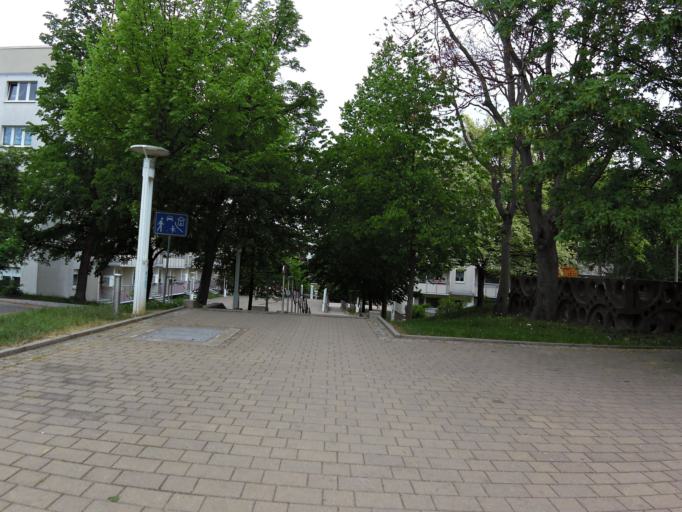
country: DE
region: Thuringia
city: Gotha
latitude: 50.9466
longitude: 10.6825
